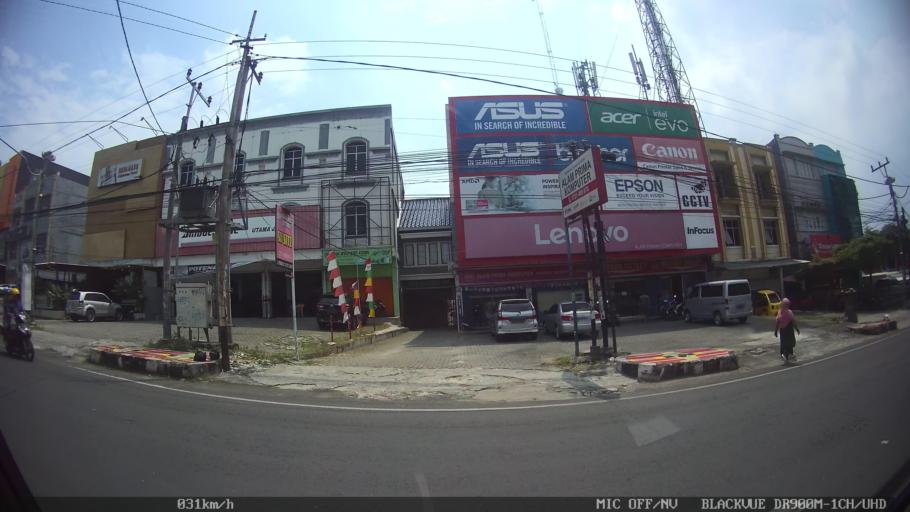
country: ID
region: Lampung
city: Bandarlampung
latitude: -5.4352
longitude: 105.2645
